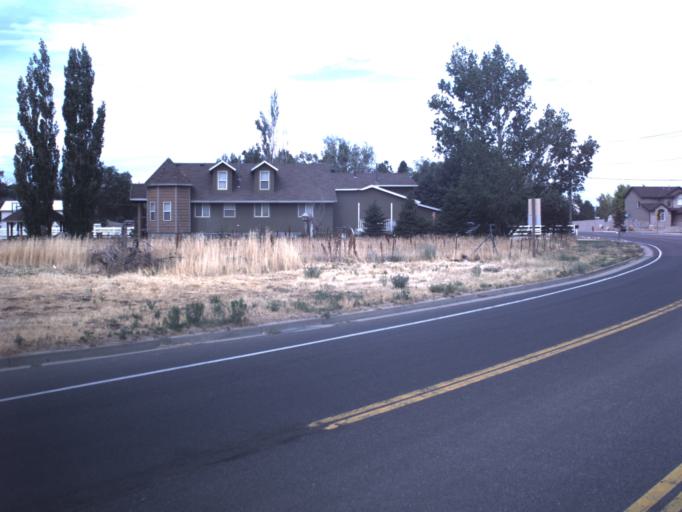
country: US
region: Utah
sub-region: Davis County
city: South Weber
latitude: 41.1318
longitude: -111.9246
